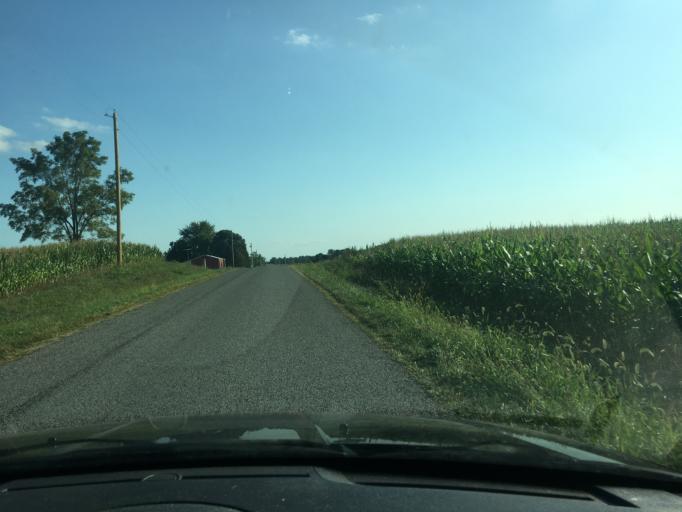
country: US
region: Ohio
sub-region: Logan County
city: West Liberty
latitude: 40.2543
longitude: -83.8037
